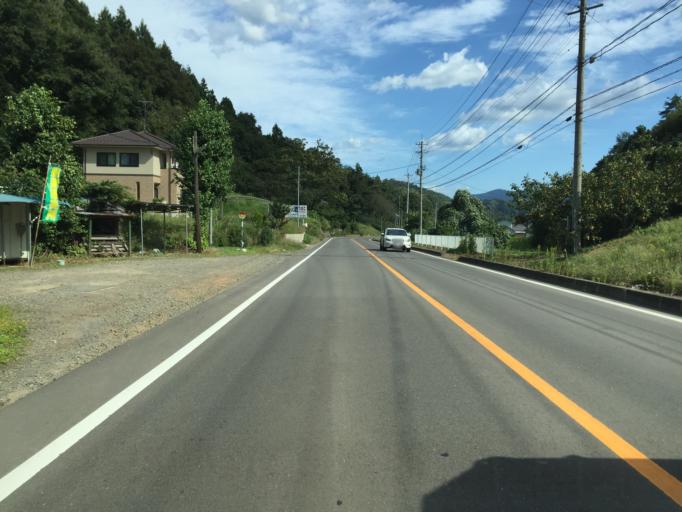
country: JP
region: Fukushima
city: Hobaramachi
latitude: 37.7884
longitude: 140.5812
